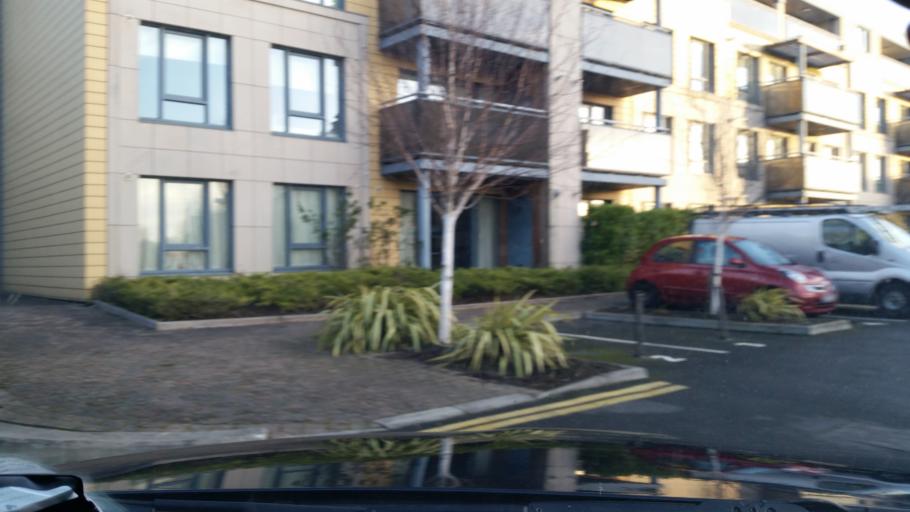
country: IE
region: Leinster
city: Drumcondra
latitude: 53.3761
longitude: -6.2450
